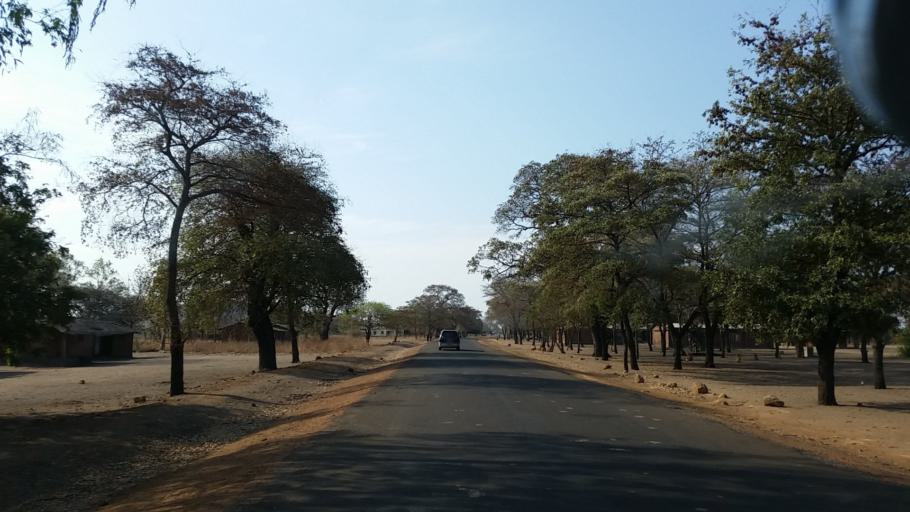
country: MW
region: Central Region
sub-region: Salima District
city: Salima
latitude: -13.7008
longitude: 34.5899
